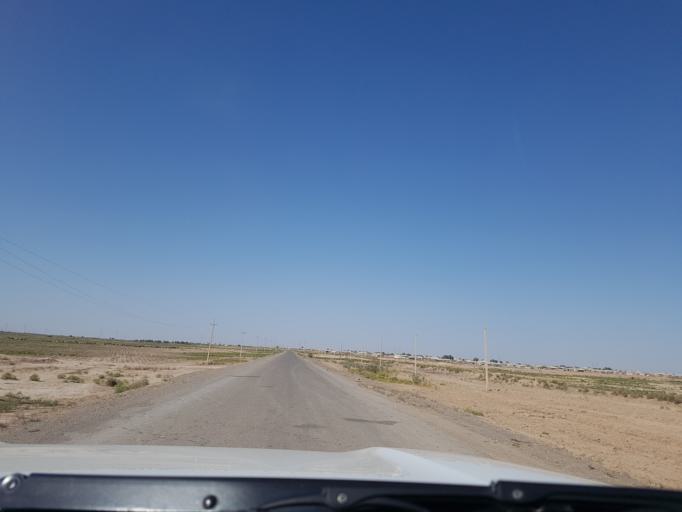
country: IR
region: Razavi Khorasan
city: Sarakhs
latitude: 36.5006
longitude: 61.2536
